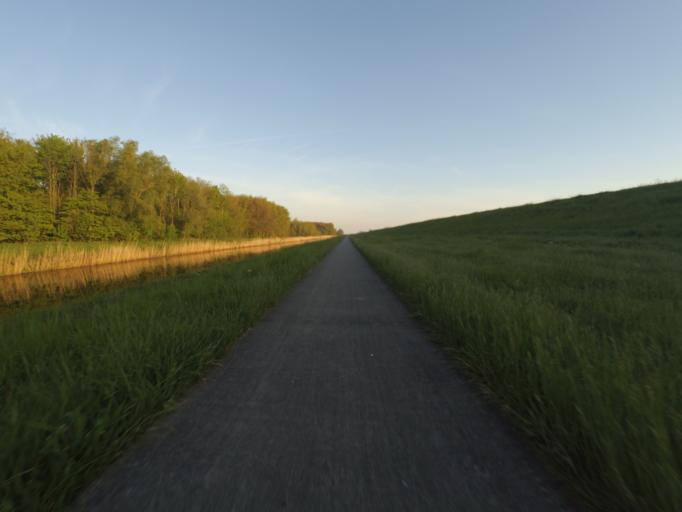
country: NL
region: Flevoland
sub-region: Gemeente Zeewolde
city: Zeewolde
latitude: 52.4018
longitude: 5.5031
